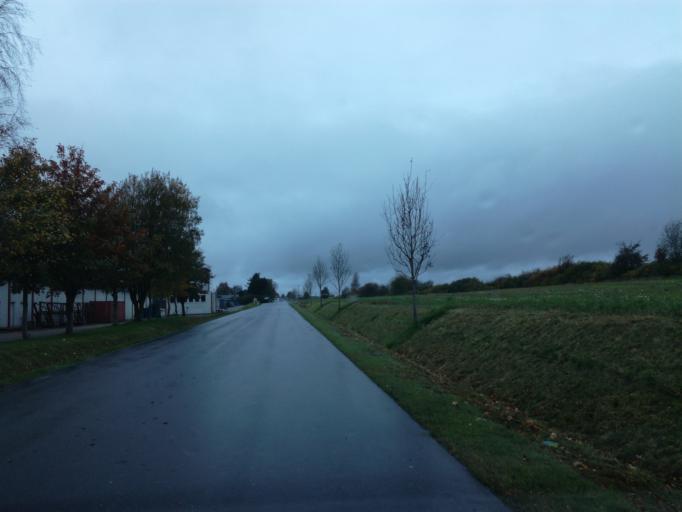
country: DK
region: South Denmark
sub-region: Vejle Kommune
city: Borkop
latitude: 55.6437
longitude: 9.6638
